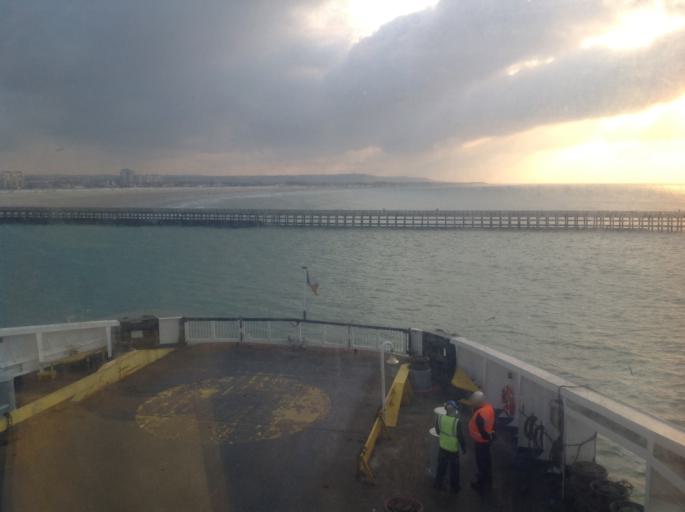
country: FR
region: Nord-Pas-de-Calais
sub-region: Departement du Pas-de-Calais
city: Calais
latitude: 50.9704
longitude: 1.8439
